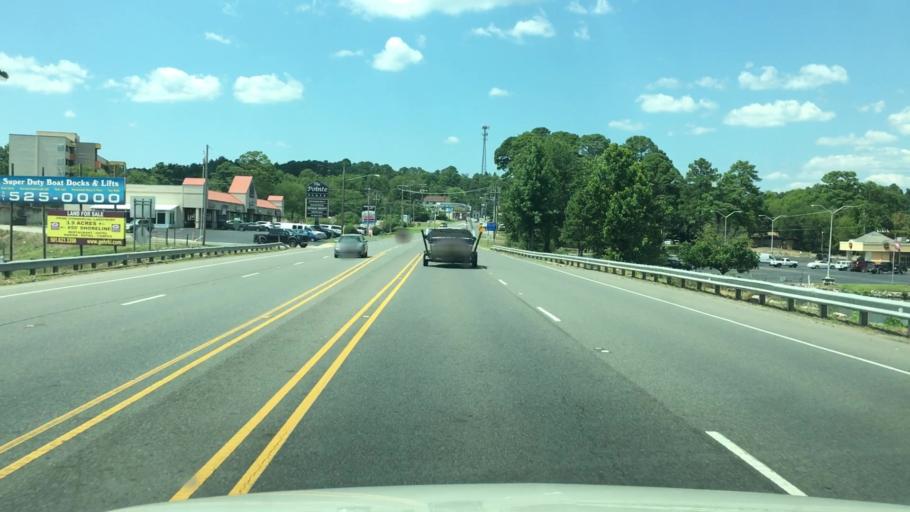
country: US
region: Arkansas
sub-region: Garland County
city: Lake Hamilton
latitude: 34.4419
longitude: -93.0889
